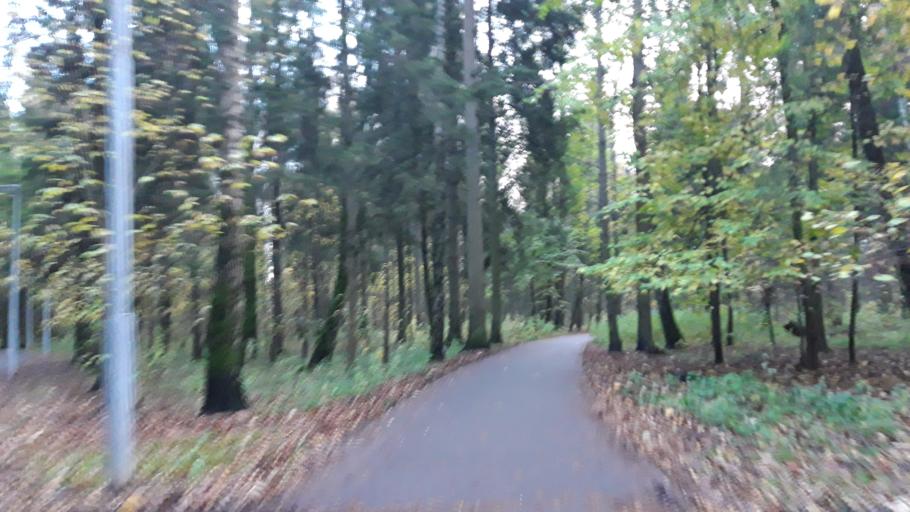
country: RU
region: Moscow
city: Zelenograd
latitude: 55.9770
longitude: 37.1947
